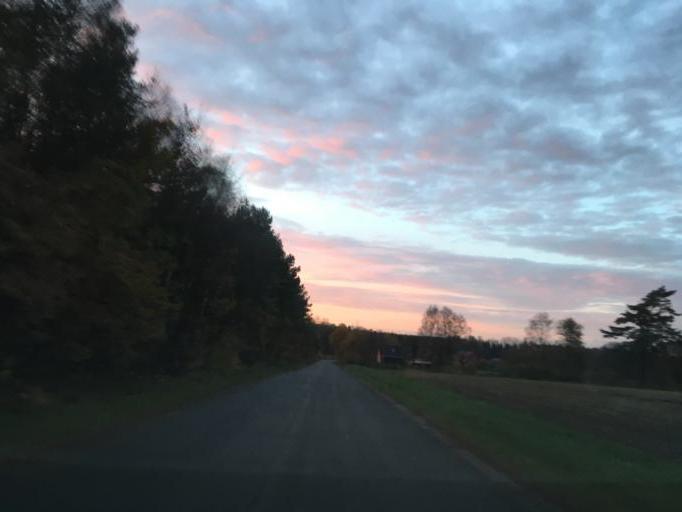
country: DE
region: Lower Saxony
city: Soderstorf
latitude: 53.1174
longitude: 10.1186
